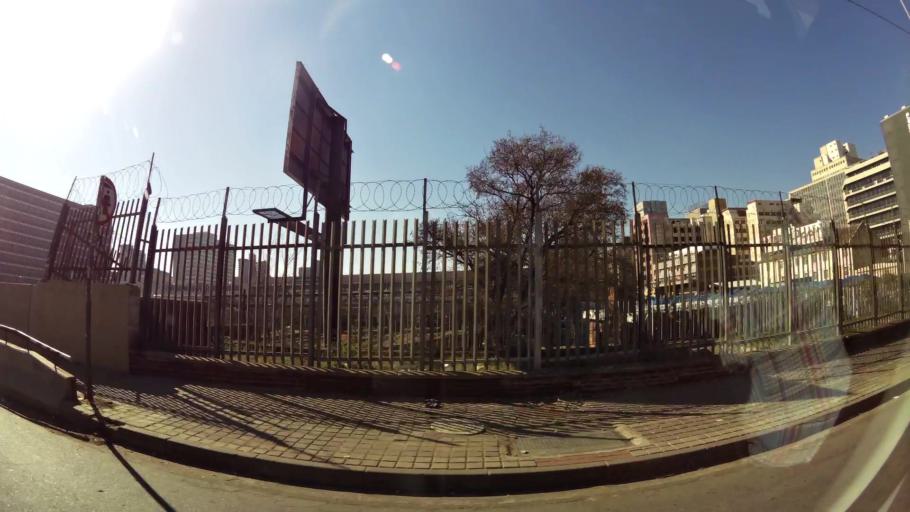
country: ZA
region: Gauteng
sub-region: City of Johannesburg Metropolitan Municipality
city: Johannesburg
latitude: -26.1984
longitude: 28.0396
